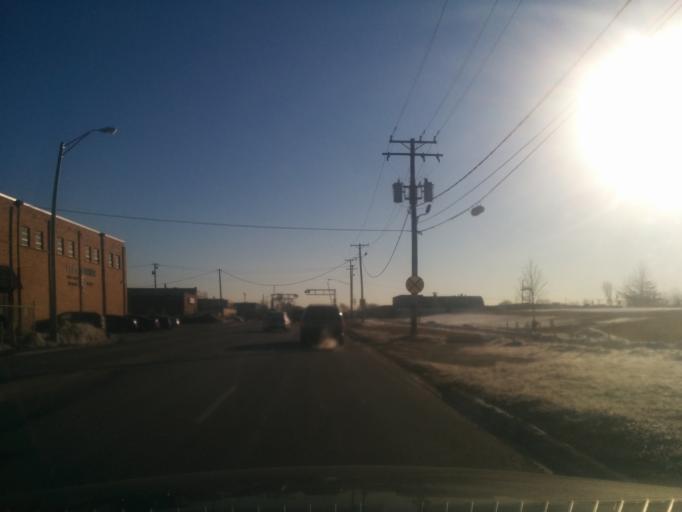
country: US
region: Illinois
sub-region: Cook County
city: Franklin Park
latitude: 41.9368
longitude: -87.8616
